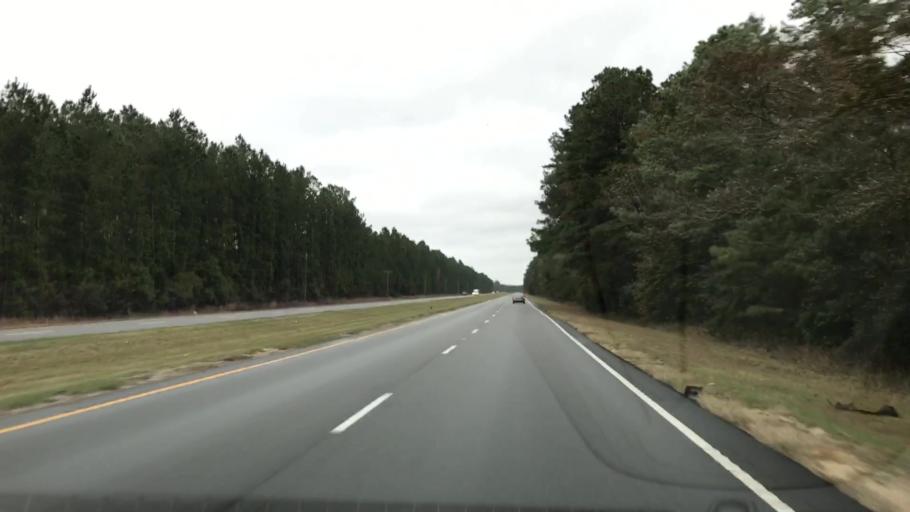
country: US
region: South Carolina
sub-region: Georgetown County
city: Georgetown
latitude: 33.2775
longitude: -79.3515
